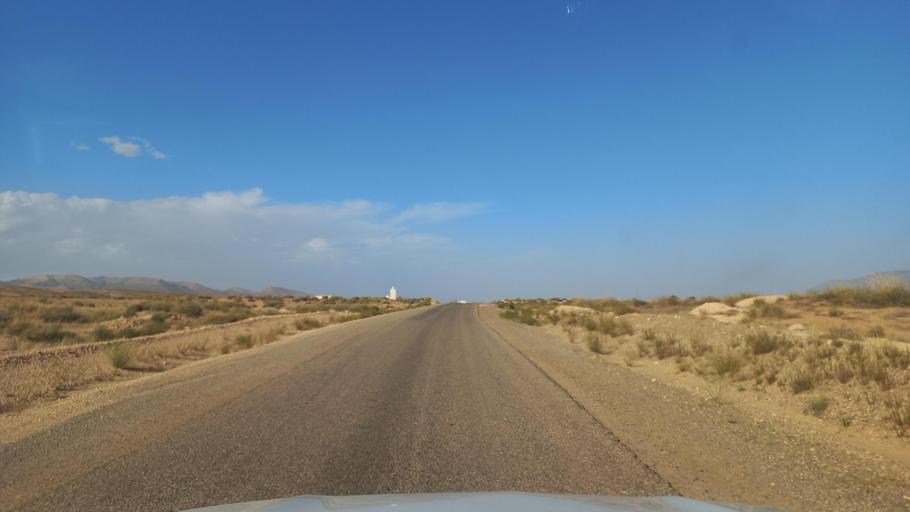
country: TN
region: Al Qasrayn
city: Sbiba
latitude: 35.3662
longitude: 9.0071
